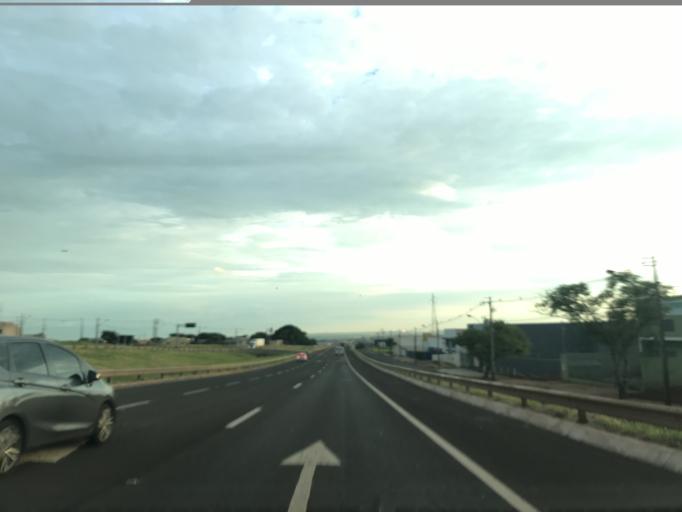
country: BR
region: Parana
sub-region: Maringa
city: Maringa
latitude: -23.4048
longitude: -51.9827
